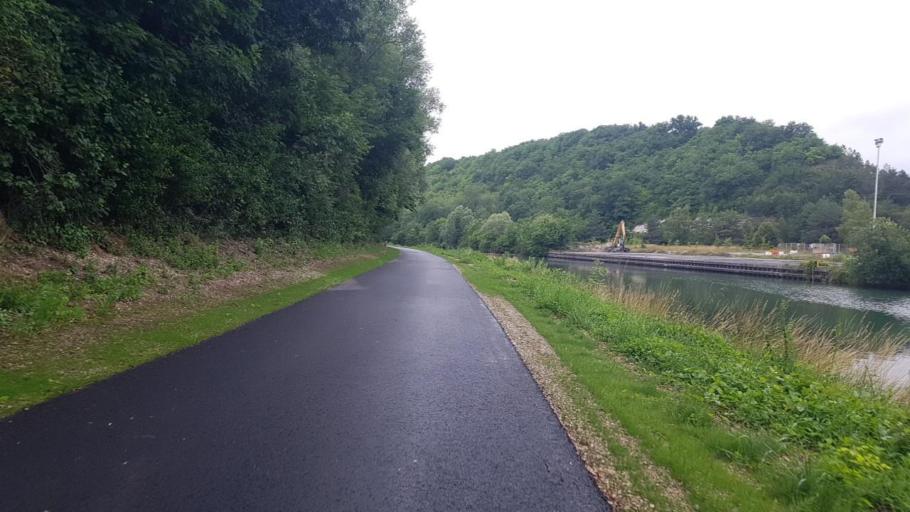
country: FR
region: Champagne-Ardenne
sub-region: Departement de la Marne
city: Vitry-le-Francois
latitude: 48.7673
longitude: 4.5585
